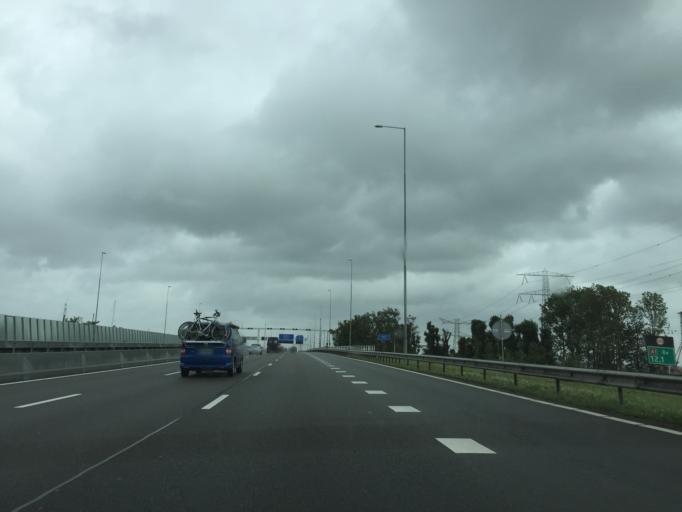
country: NL
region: North Holland
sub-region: Gemeente Weesp
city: Weesp
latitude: 52.3273
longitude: 5.0618
